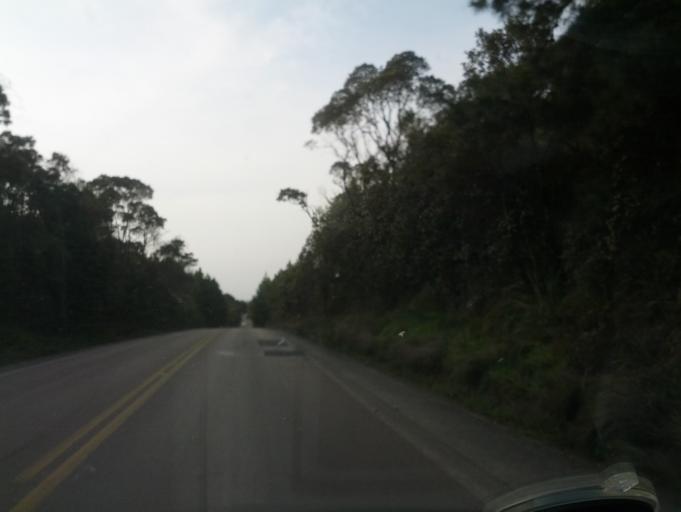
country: BR
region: Santa Catarina
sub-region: Otacilio Costa
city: Otacilio Costa
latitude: -27.3913
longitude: -50.1341
